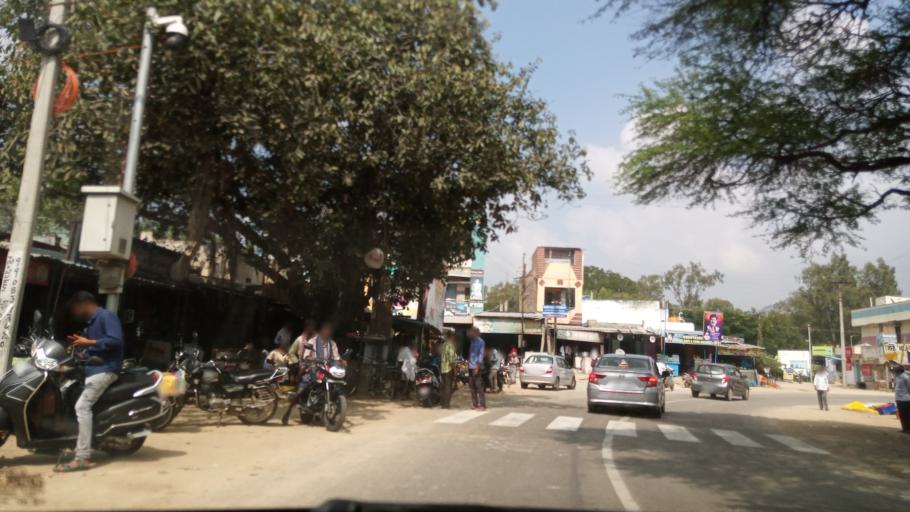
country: IN
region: Andhra Pradesh
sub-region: Chittoor
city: Madanapalle
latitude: 13.6426
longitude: 78.5545
